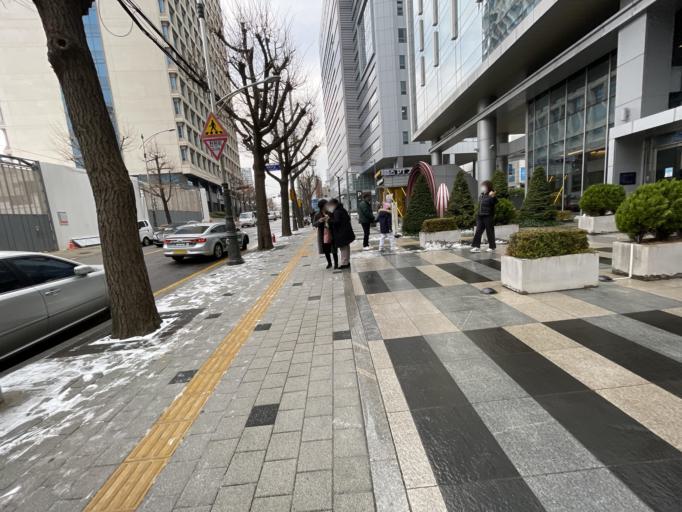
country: KR
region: Seoul
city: Seoul
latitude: 37.5646
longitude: 126.9907
